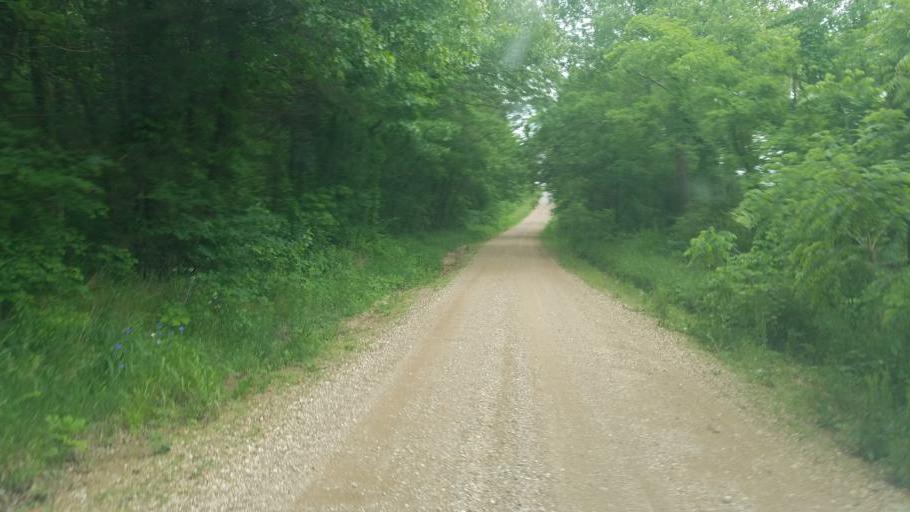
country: US
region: Missouri
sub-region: Moniteau County
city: California
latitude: 38.6219
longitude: -92.6250
